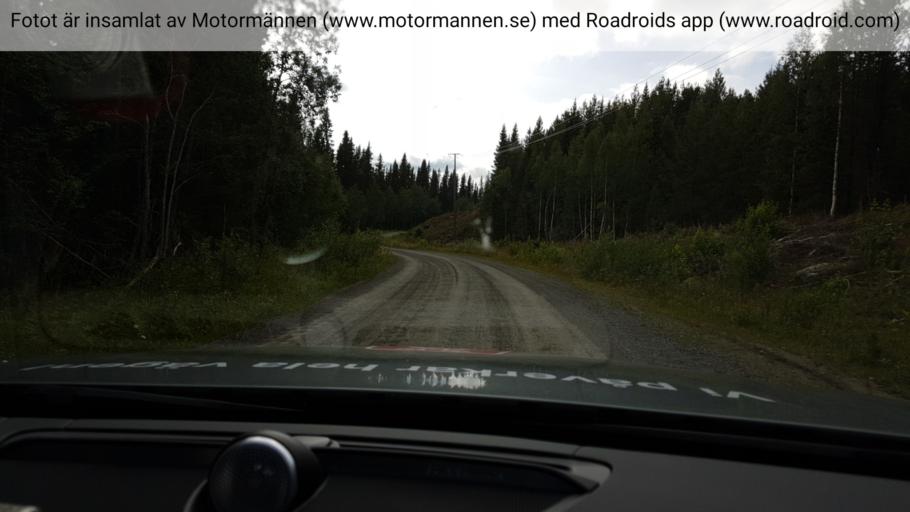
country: SE
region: Jaemtland
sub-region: Stroemsunds Kommun
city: Stroemsund
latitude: 64.5328
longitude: 15.2860
